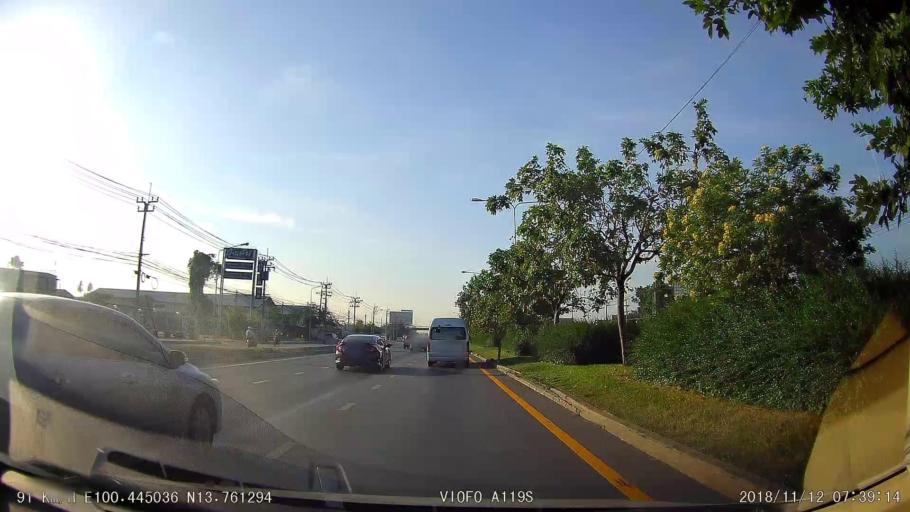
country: TH
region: Bangkok
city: Taling Chan
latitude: 13.7610
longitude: 100.4451
